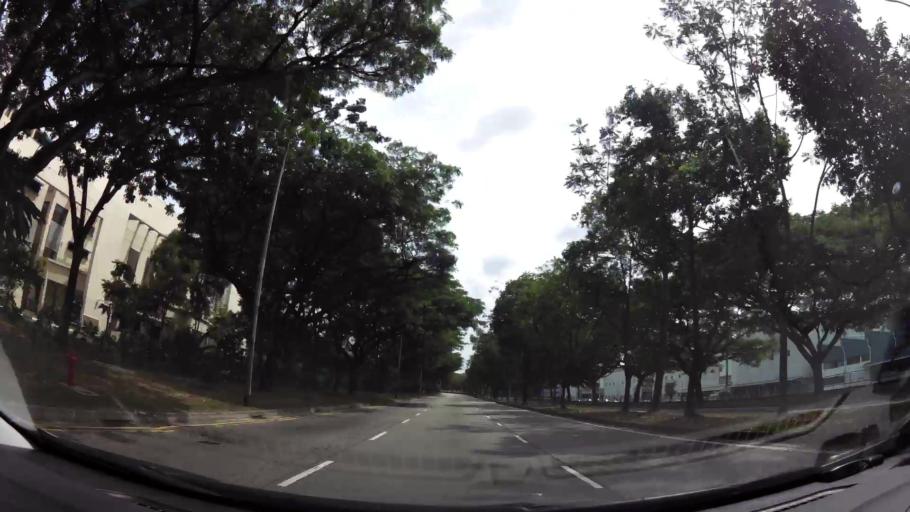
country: MY
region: Johor
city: Johor Bahru
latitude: 1.3349
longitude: 103.7020
